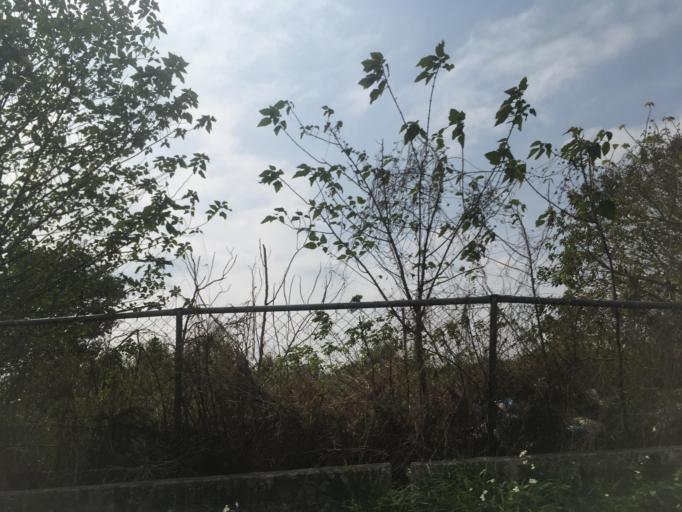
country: TW
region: Taiwan
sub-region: Yunlin
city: Douliu
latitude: 23.6923
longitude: 120.4601
